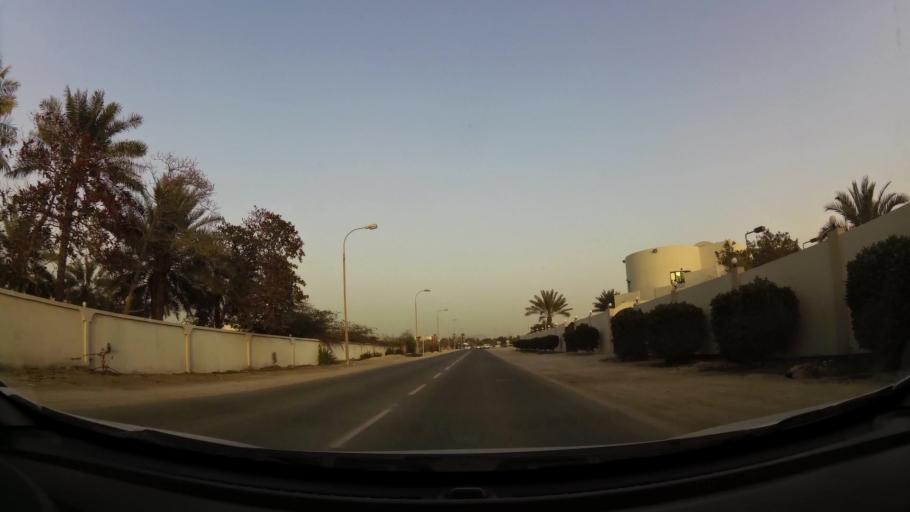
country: BH
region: Manama
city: Jidd Hafs
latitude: 26.1969
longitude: 50.4745
